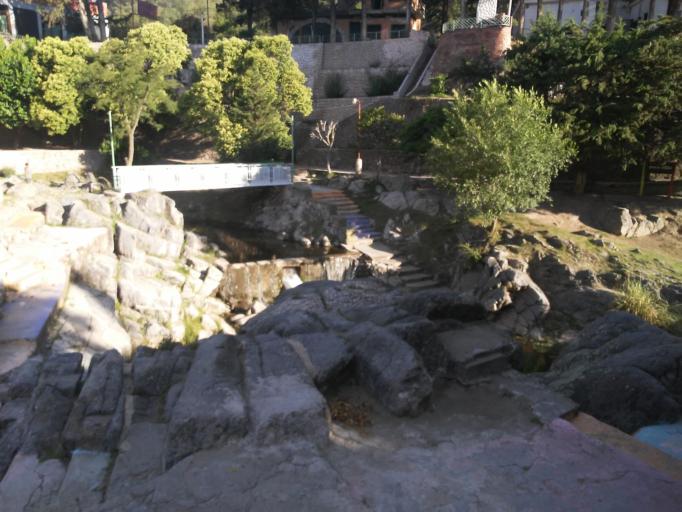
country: AR
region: San Luis
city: La Punta
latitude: -33.2505
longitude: -66.1923
